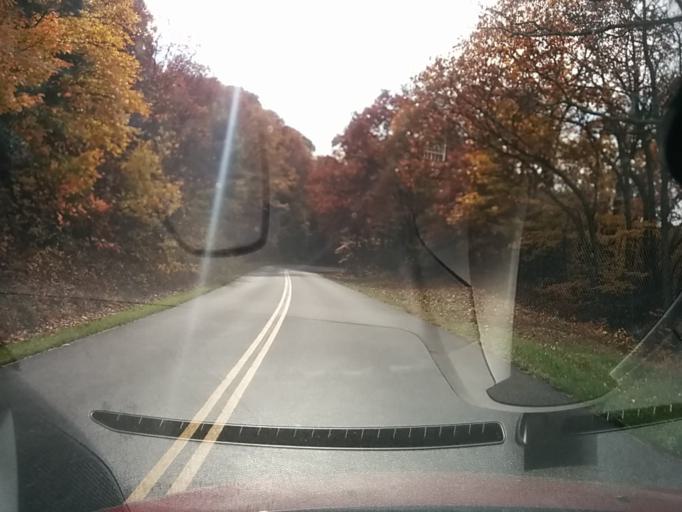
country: US
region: Virginia
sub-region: Nelson County
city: Nellysford
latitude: 37.8972
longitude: -78.9899
